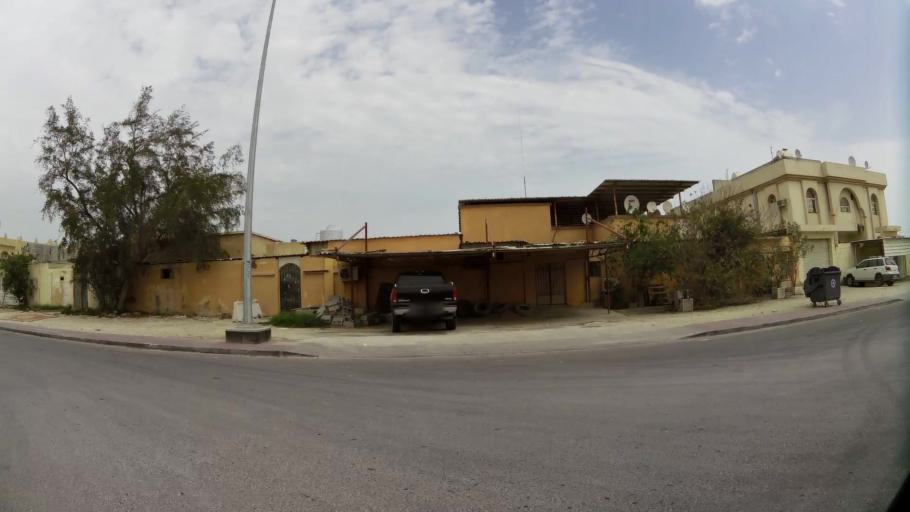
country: QA
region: Baladiyat ar Rayyan
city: Ar Rayyan
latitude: 25.3269
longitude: 51.4693
